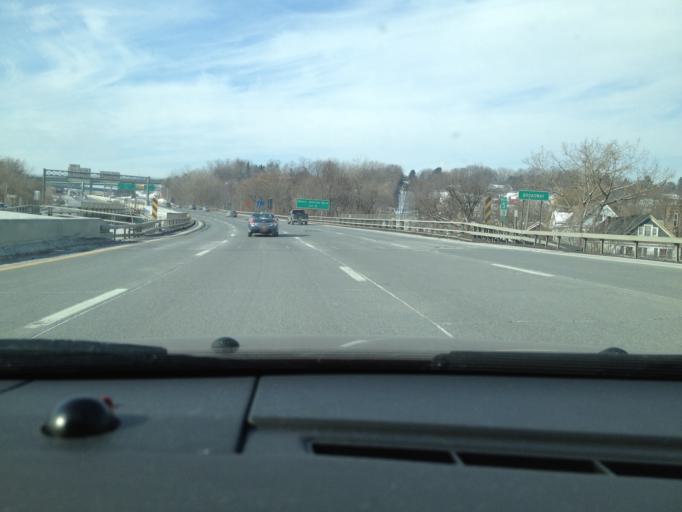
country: US
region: New York
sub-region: Albany County
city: Albany
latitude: 42.6701
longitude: -73.7383
